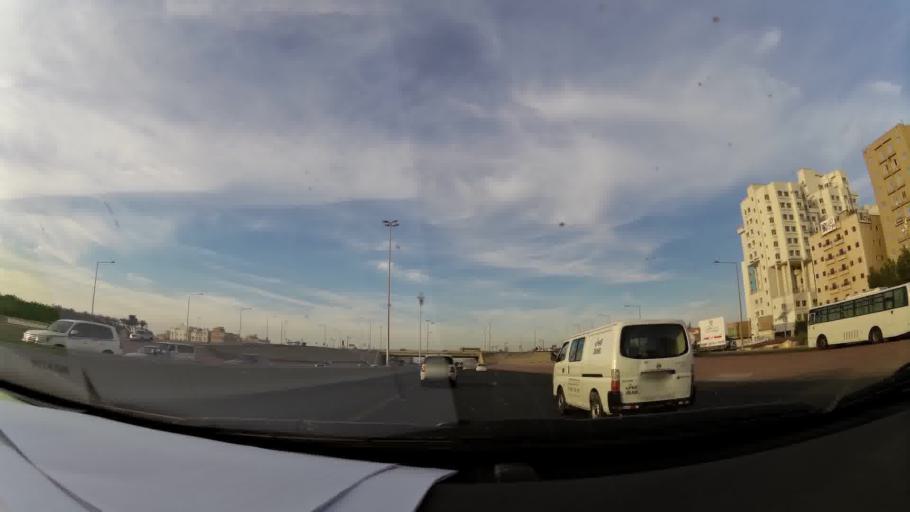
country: KW
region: Al Ahmadi
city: Al Fintas
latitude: 29.1582
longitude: 48.1111
